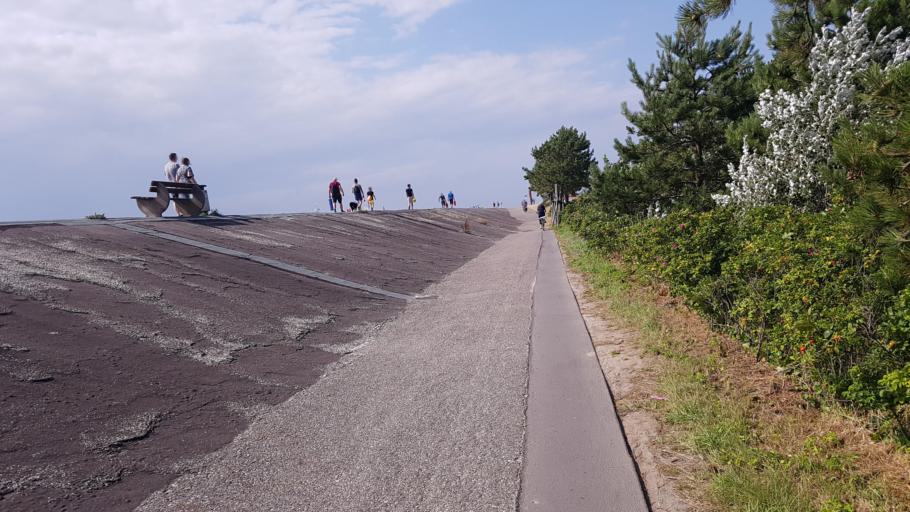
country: DE
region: Schleswig-Holstein
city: Sankt Peter-Ording
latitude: 54.3125
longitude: 8.6058
